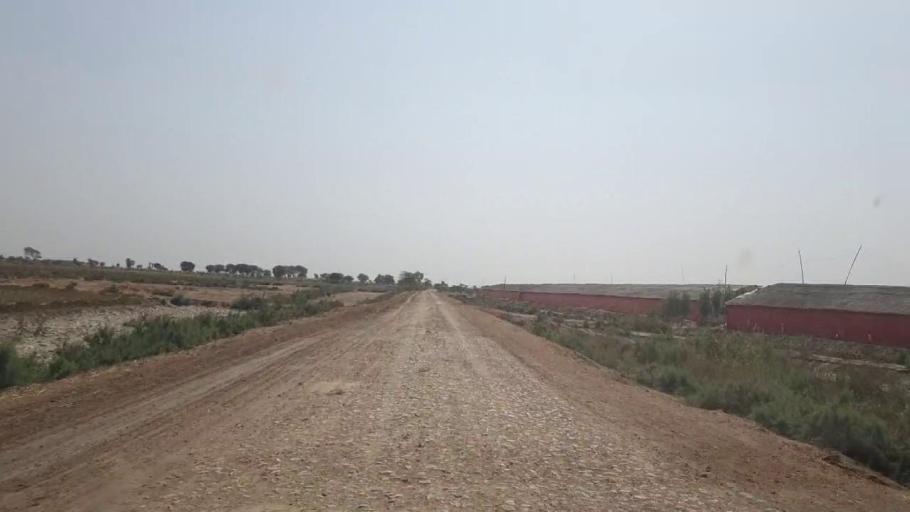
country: PK
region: Sindh
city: Jati
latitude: 24.4243
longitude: 68.5524
